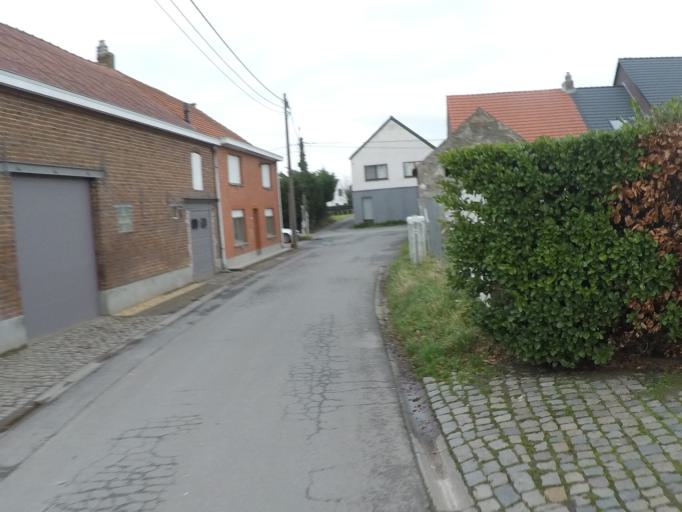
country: BE
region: Flanders
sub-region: Provincie Vlaams-Brabant
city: Merchtem
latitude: 50.9943
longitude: 4.2436
